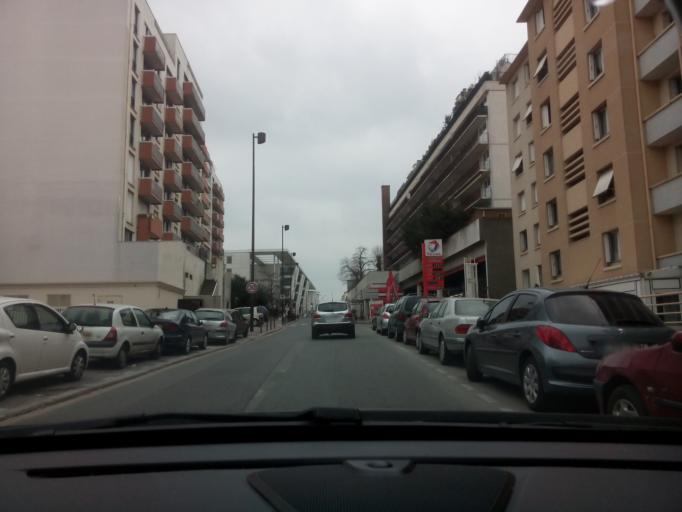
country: FR
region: Ile-de-France
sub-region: Departement du Val-de-Marne
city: Charenton-le-Pont
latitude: 48.8214
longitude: 2.4018
